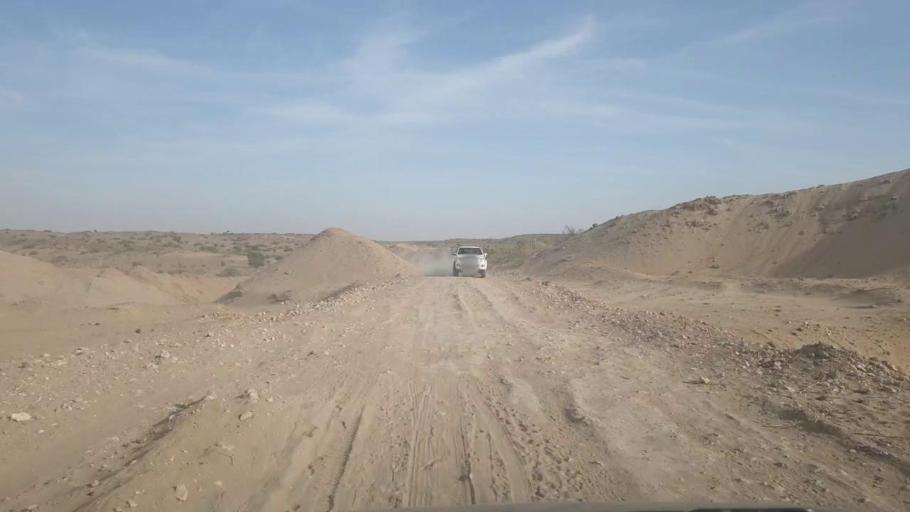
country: PK
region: Sindh
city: Nabisar
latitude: 25.0631
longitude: 69.6554
